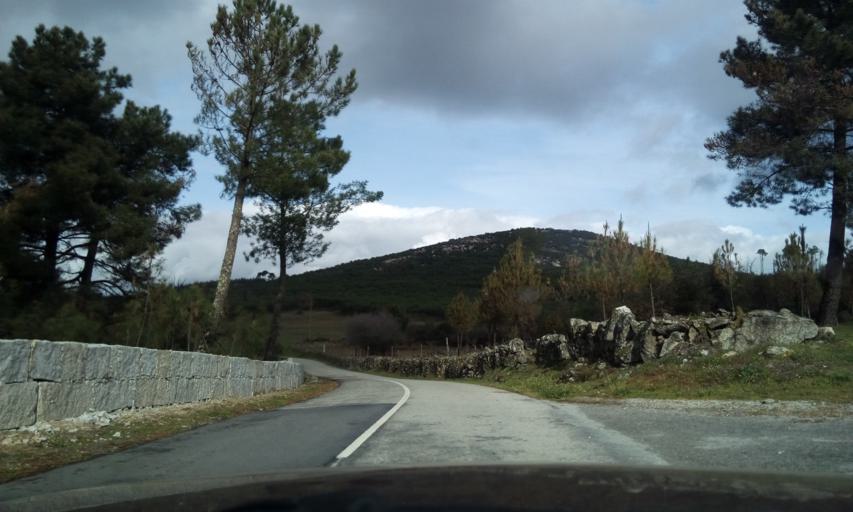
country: PT
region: Guarda
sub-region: Fornos de Algodres
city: Fornos de Algodres
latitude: 40.6575
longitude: -7.5857
